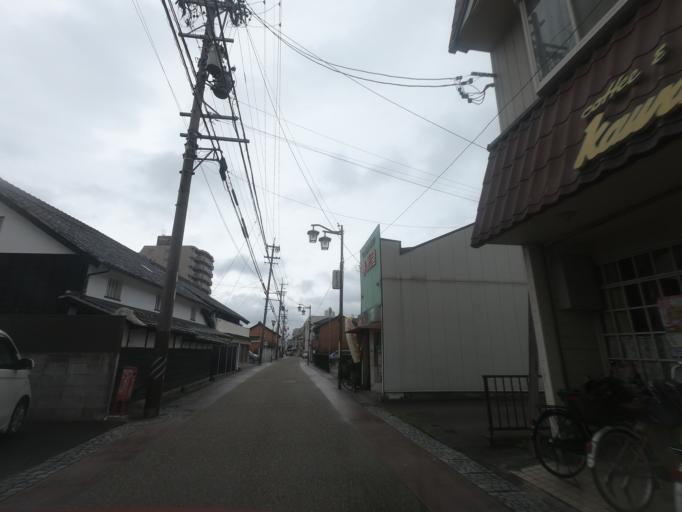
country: JP
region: Aichi
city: Kasugai
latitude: 35.2466
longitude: 136.9770
